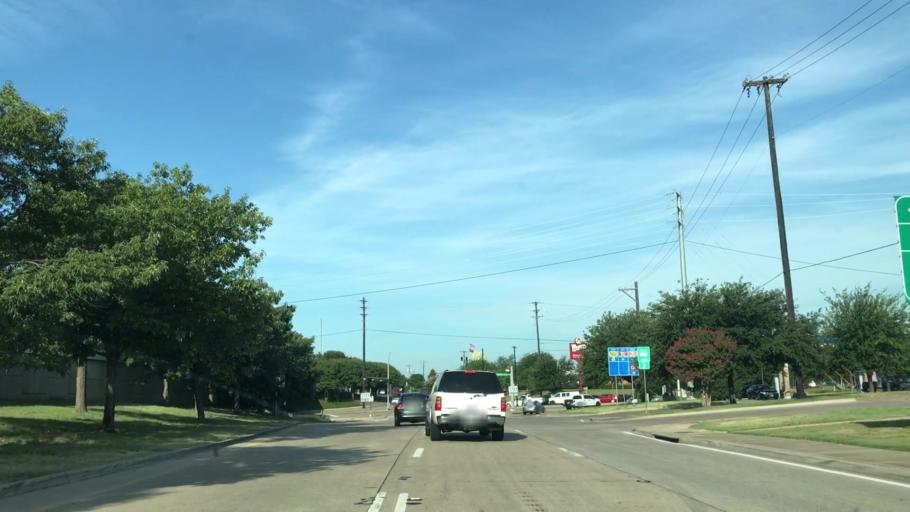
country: US
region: Texas
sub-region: Dallas County
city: Sunnyvale
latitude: 32.8410
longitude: -96.5942
